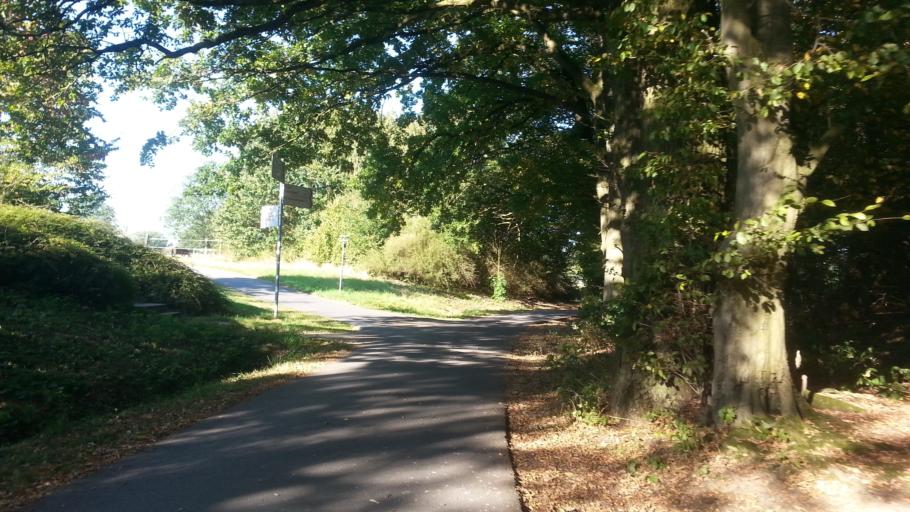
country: DE
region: North Rhine-Westphalia
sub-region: Regierungsbezirk Munster
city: Muenster
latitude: 51.9416
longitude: 7.5890
